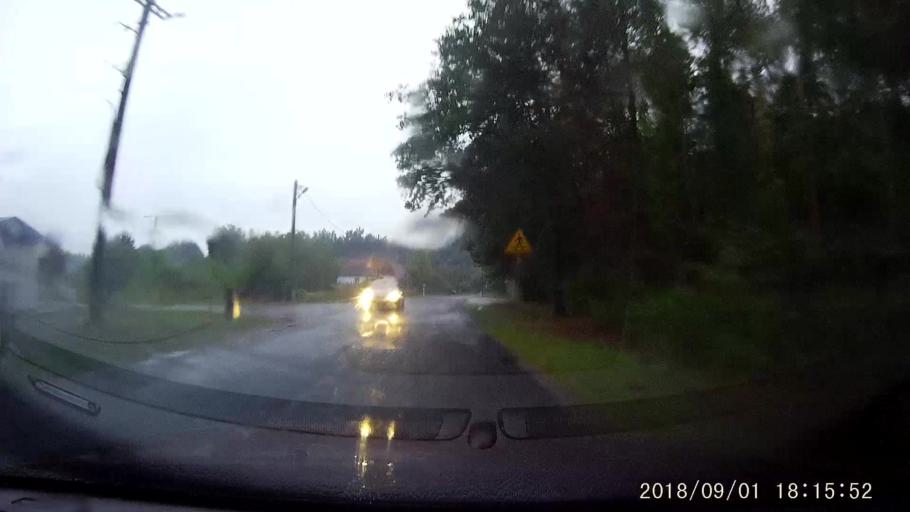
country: PL
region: Lower Silesian Voivodeship
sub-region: Powiat zgorzelecki
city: Piensk
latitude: 51.2777
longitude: 15.0568
